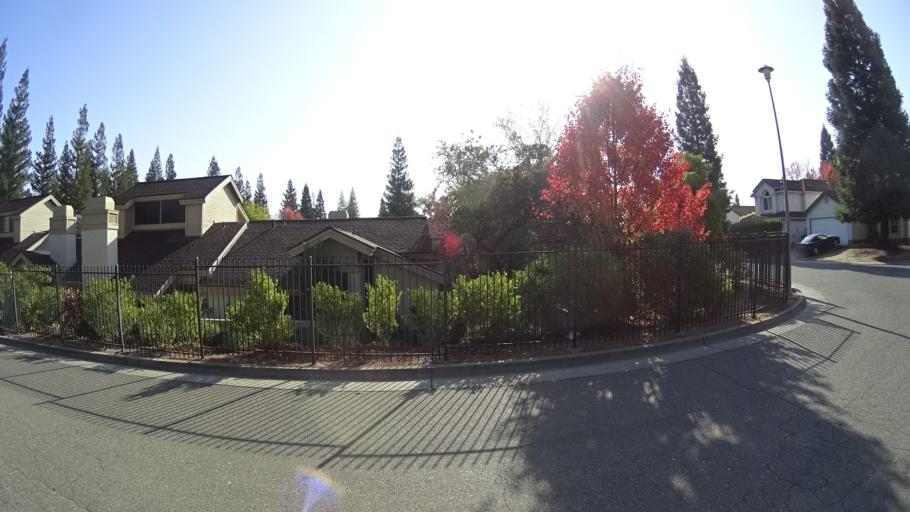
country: US
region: California
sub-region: Sacramento County
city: Citrus Heights
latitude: 38.7033
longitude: -121.2489
